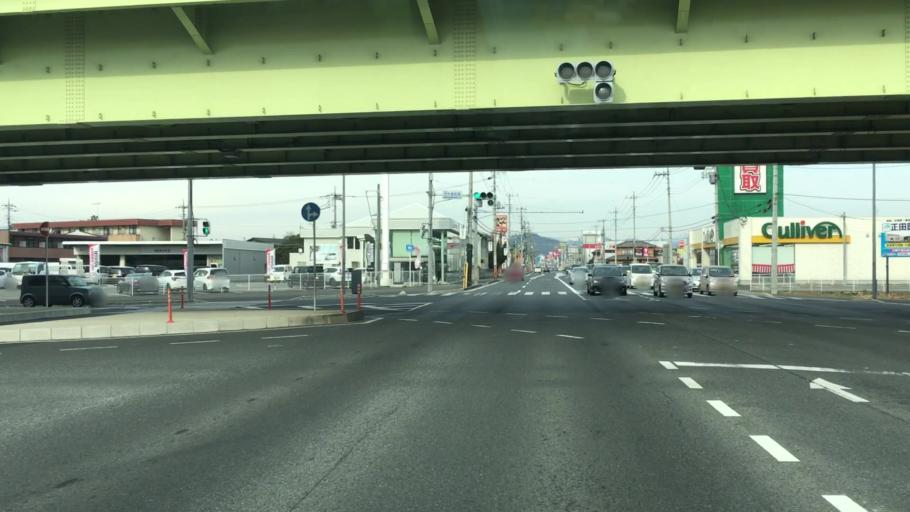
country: JP
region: Gunma
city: Ota
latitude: 36.2691
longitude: 139.3771
